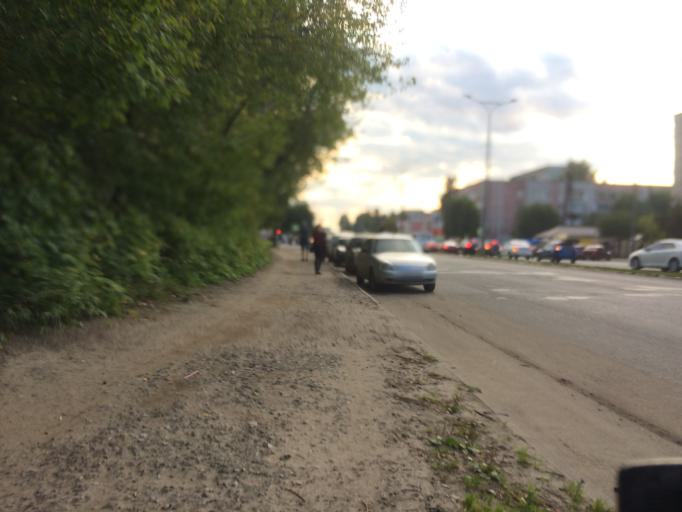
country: RU
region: Mariy-El
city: Medvedevo
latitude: 56.6415
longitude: 47.8469
